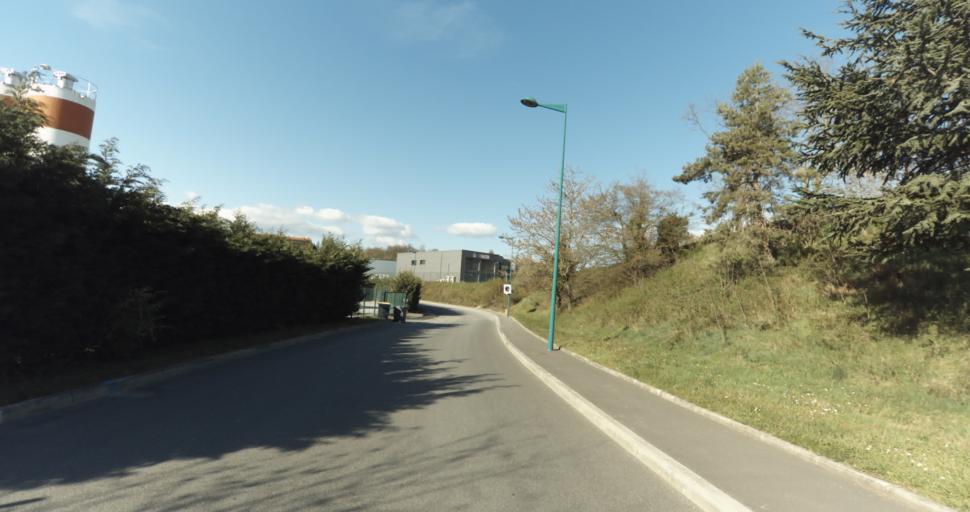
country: FR
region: Rhone-Alpes
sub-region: Departement de la Loire
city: La Talaudiere
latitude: 45.4653
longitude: 4.4281
